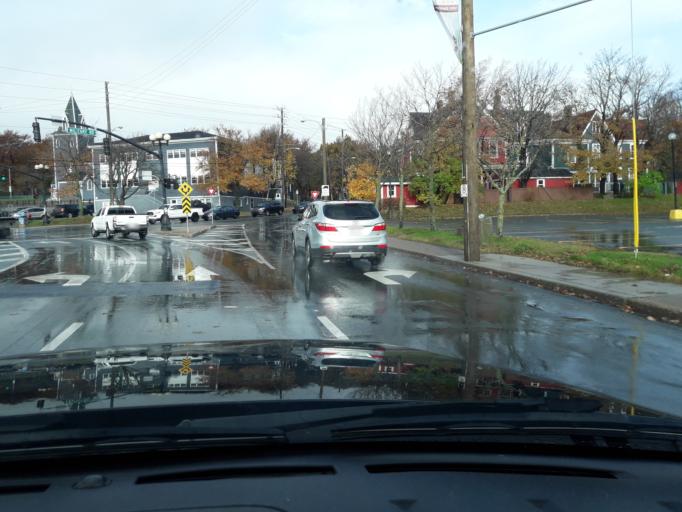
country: CA
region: Newfoundland and Labrador
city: St. John's
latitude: 47.5711
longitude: -52.7012
